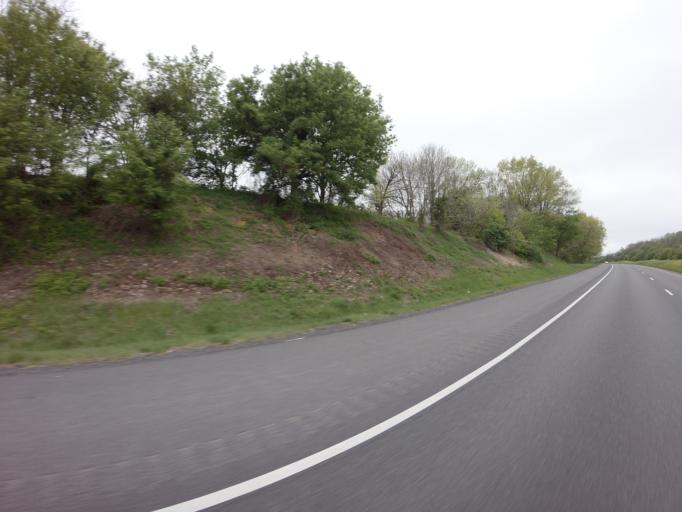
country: US
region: Maryland
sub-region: Washington County
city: Robinwood
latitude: 39.5972
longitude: -77.6595
